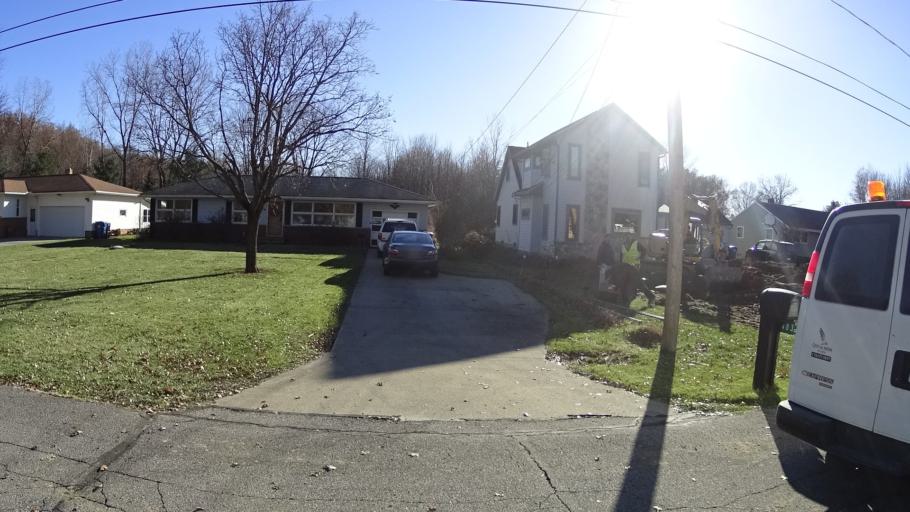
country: US
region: Ohio
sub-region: Lorain County
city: Avon Center
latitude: 41.4476
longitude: -81.9871
